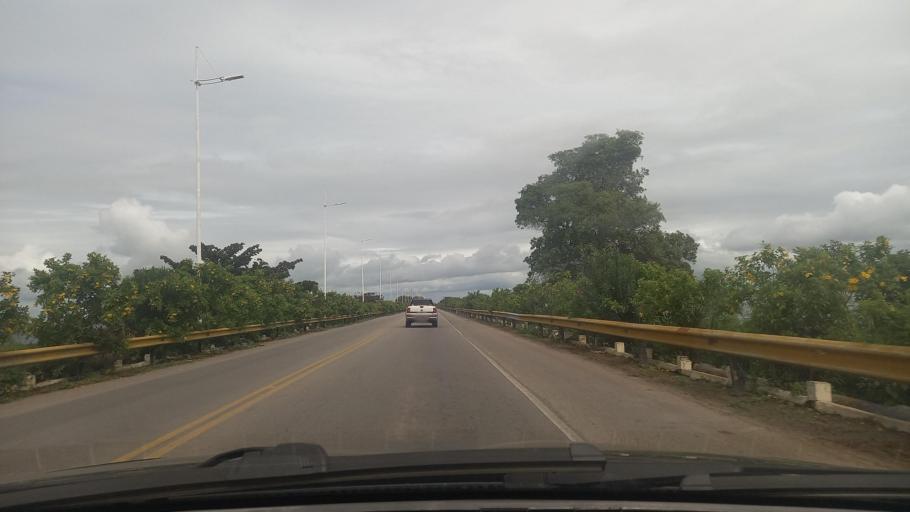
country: BR
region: Bahia
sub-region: Paulo Afonso
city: Paulo Afonso
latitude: -9.4136
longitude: -38.2345
